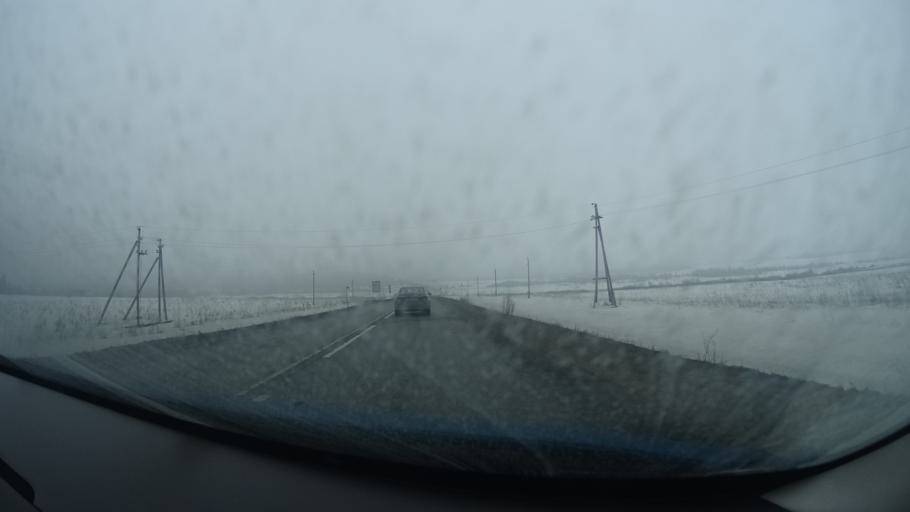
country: RU
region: Perm
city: Kuyeda
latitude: 56.4697
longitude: 55.7105
